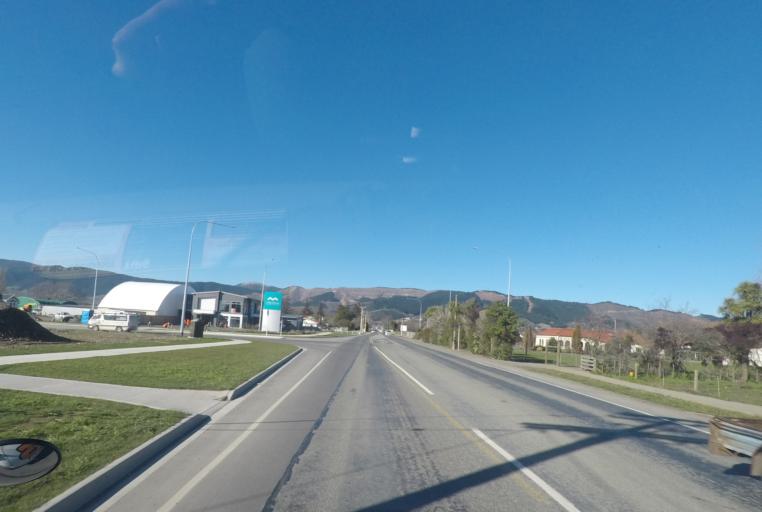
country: NZ
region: Tasman
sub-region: Tasman District
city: Richmond
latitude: -41.3294
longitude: 173.1738
